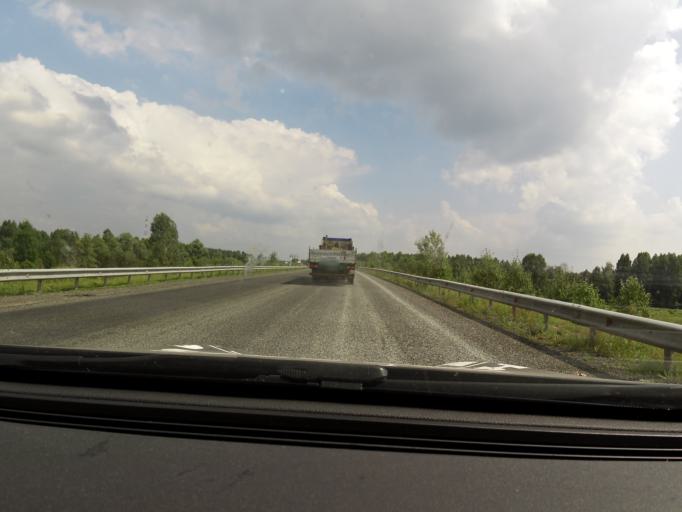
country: RU
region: Sverdlovsk
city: Ufimskiy
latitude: 56.7653
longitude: 58.1372
